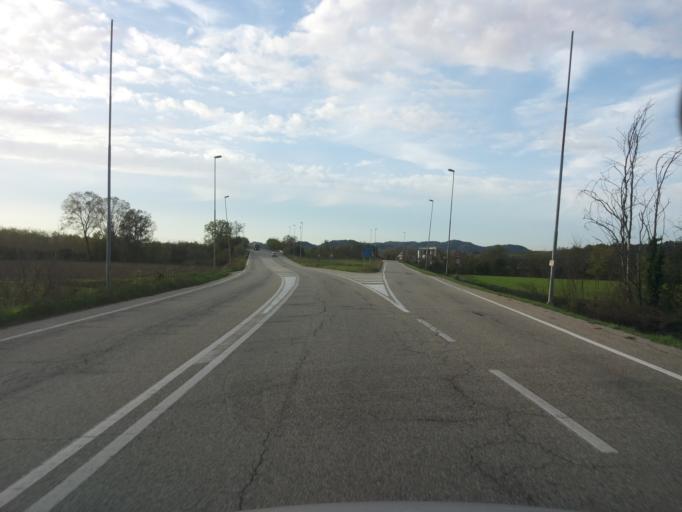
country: IT
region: Piedmont
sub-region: Provincia di Alessandria
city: Cereseto
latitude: 45.1121
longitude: 8.3261
